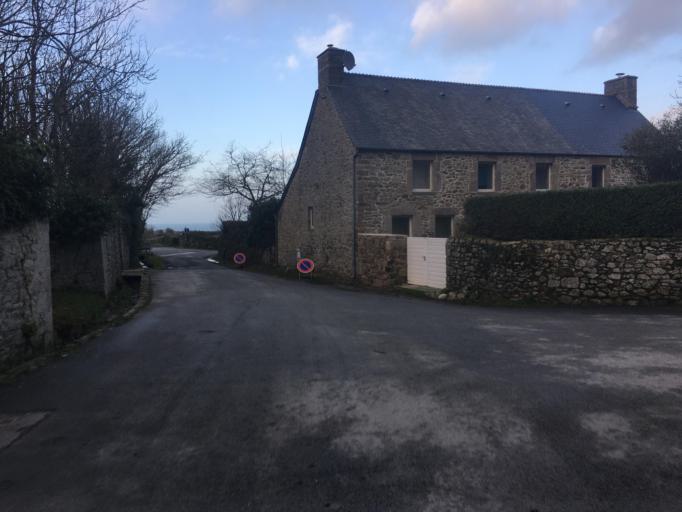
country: FR
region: Lower Normandy
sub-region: Departement de la Manche
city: Beaumont-Hague
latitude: 49.7143
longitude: -1.9220
